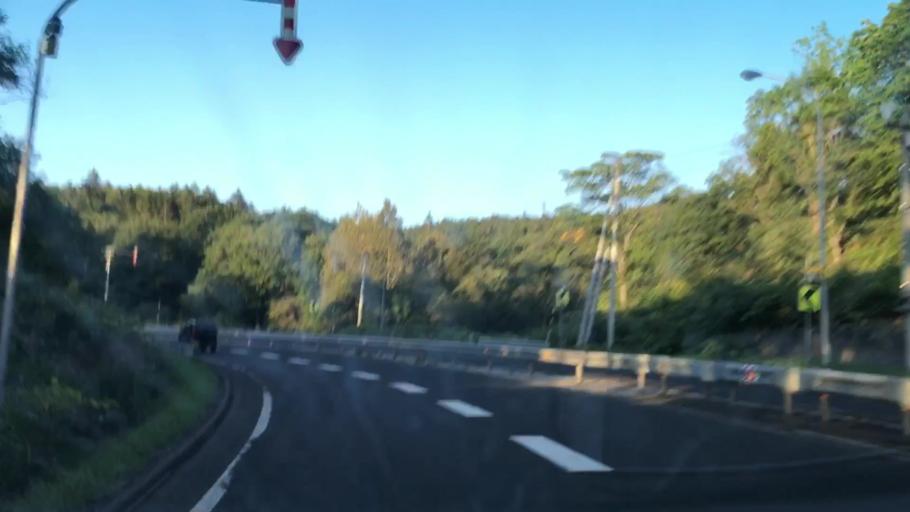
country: JP
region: Hokkaido
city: Otaru
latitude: 42.8454
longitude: 141.0697
